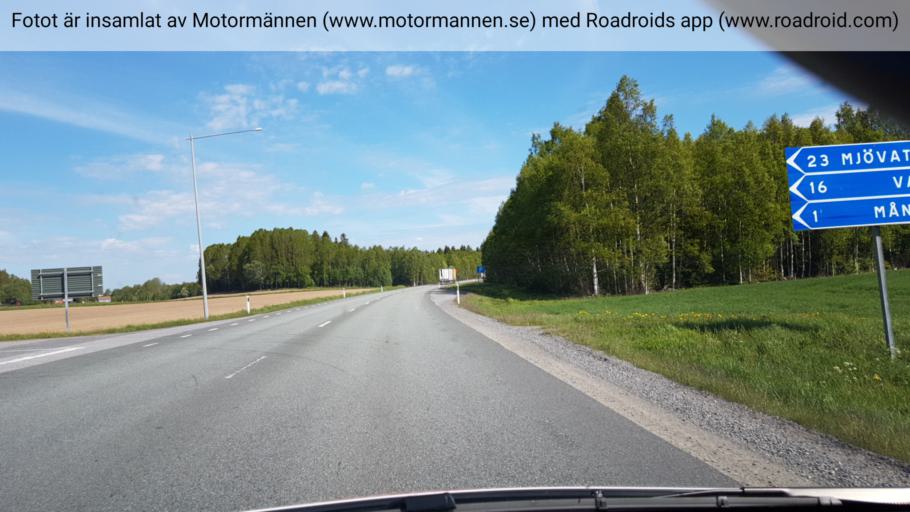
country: SE
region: Vaesterbotten
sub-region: Skelleftea Kommun
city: Burea
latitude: 64.3903
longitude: 21.2978
